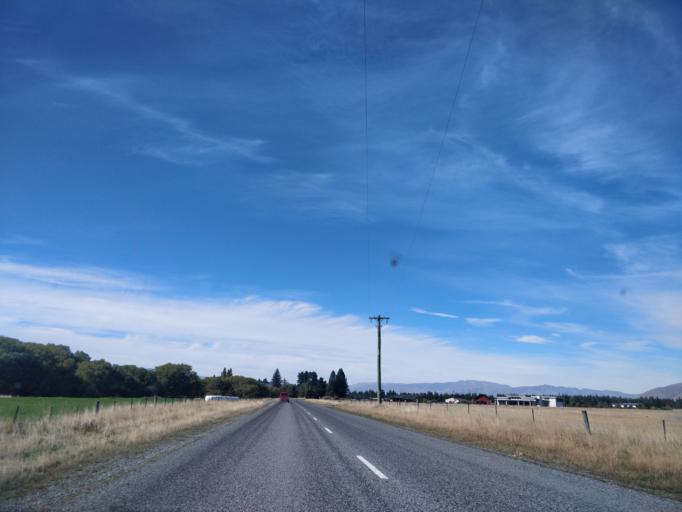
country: NZ
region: Otago
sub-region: Queenstown-Lakes District
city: Wanaka
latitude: -44.2374
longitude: 170.0768
